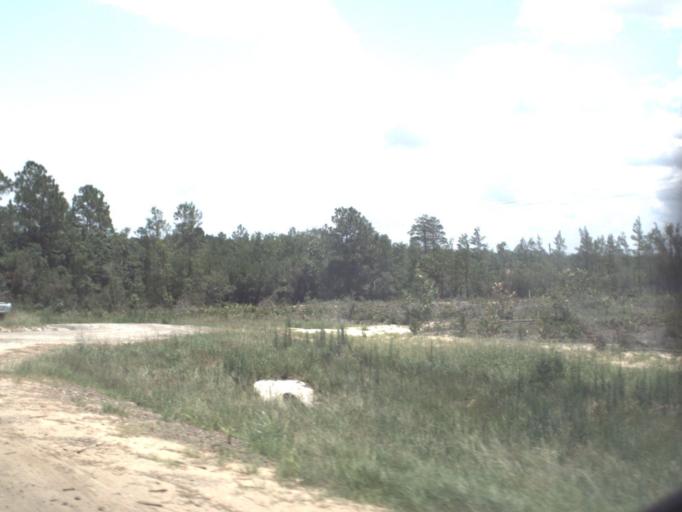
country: US
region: Florida
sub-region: Walton County
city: Freeport
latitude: 30.5209
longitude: -86.1085
